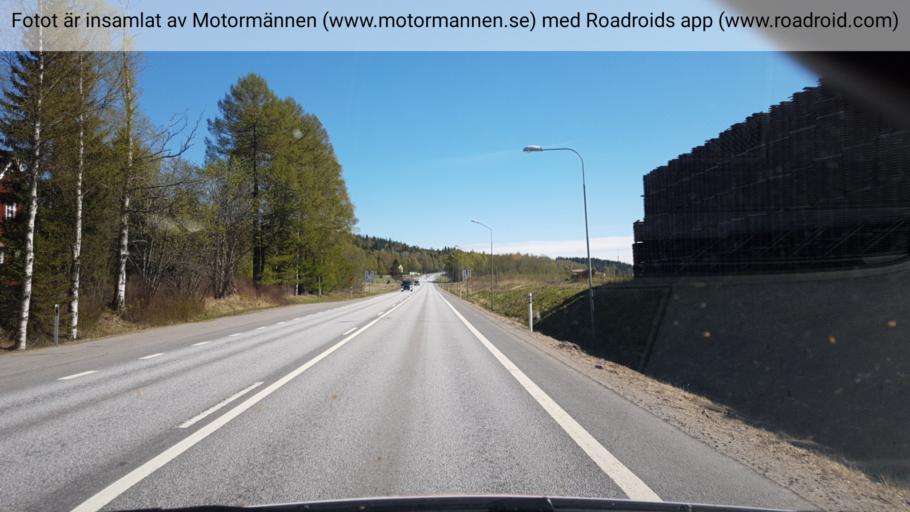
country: SE
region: Vaesterbotten
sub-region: Vannas Kommun
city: Vannasby
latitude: 63.9175
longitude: 19.8760
